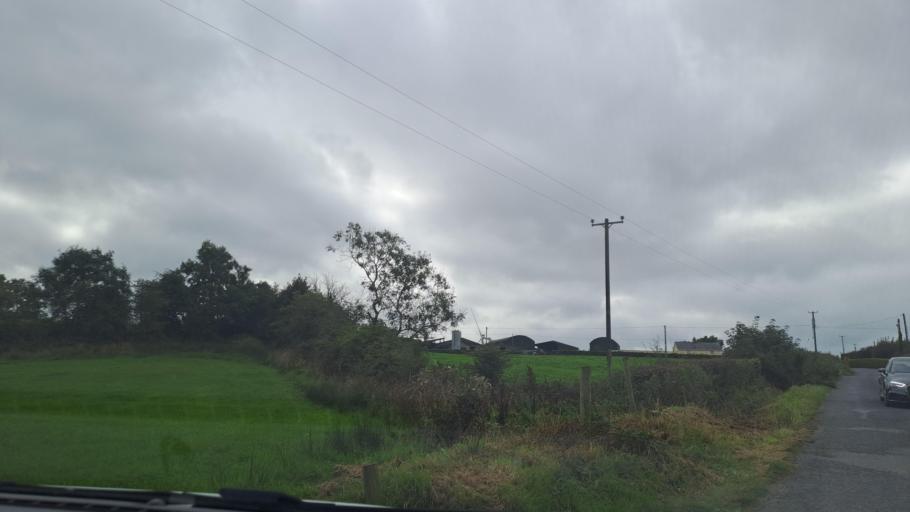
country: IE
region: Ulster
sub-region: An Cabhan
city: Kingscourt
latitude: 53.9622
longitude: -6.8757
